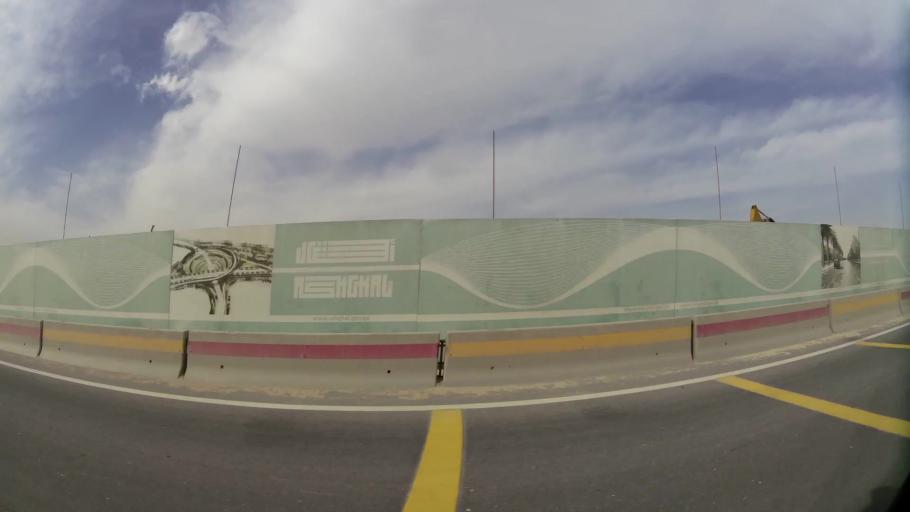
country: QA
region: Baladiyat ar Rayyan
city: Ar Rayyan
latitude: 25.3072
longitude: 51.4053
